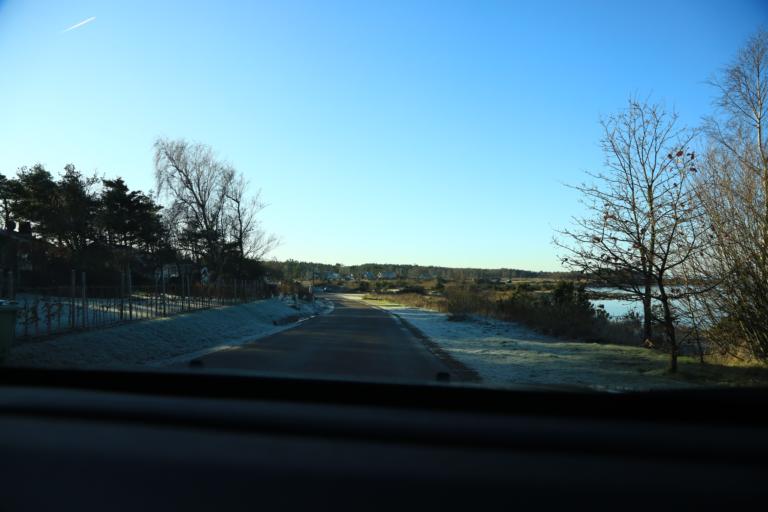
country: SE
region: Halland
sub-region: Kungsbacka Kommun
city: Frillesas
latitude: 57.2018
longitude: 12.1836
